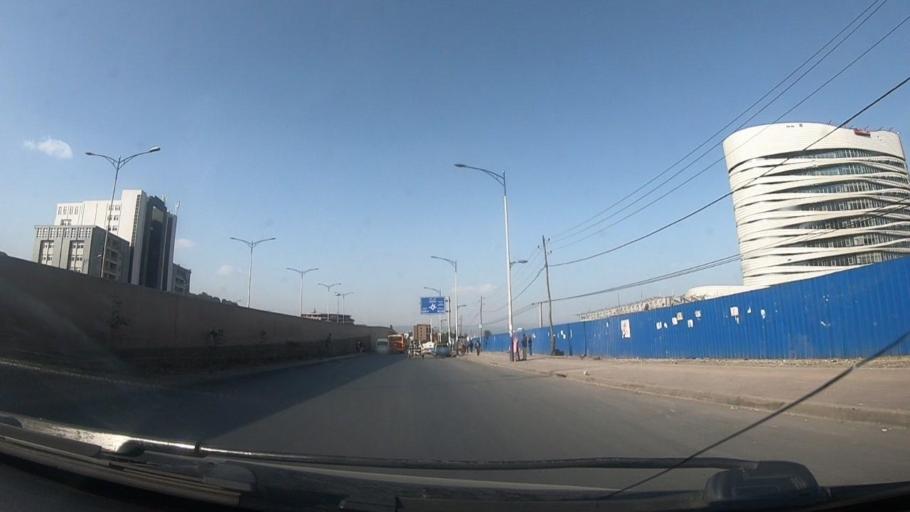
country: ET
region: Adis Abeba
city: Addis Ababa
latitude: 8.9346
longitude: 38.7345
